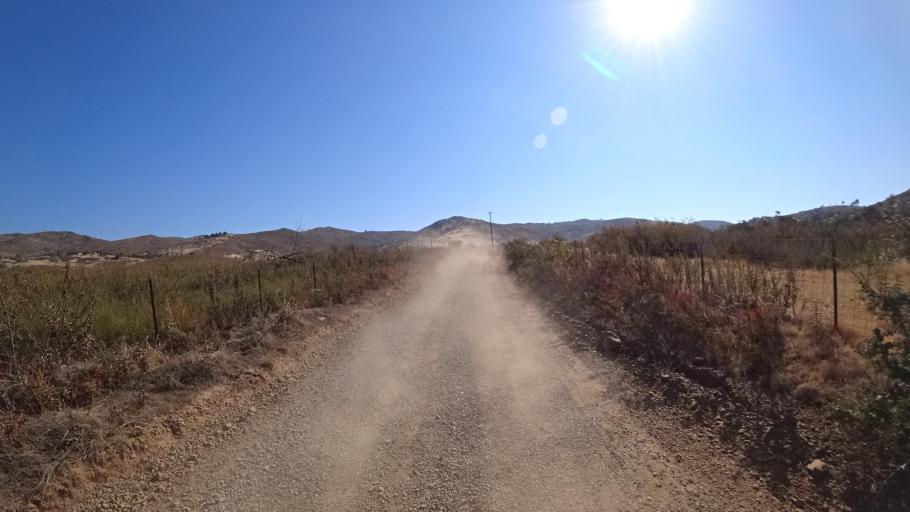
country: US
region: California
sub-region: Mariposa County
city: Mariposa
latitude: 37.6183
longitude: -120.2231
